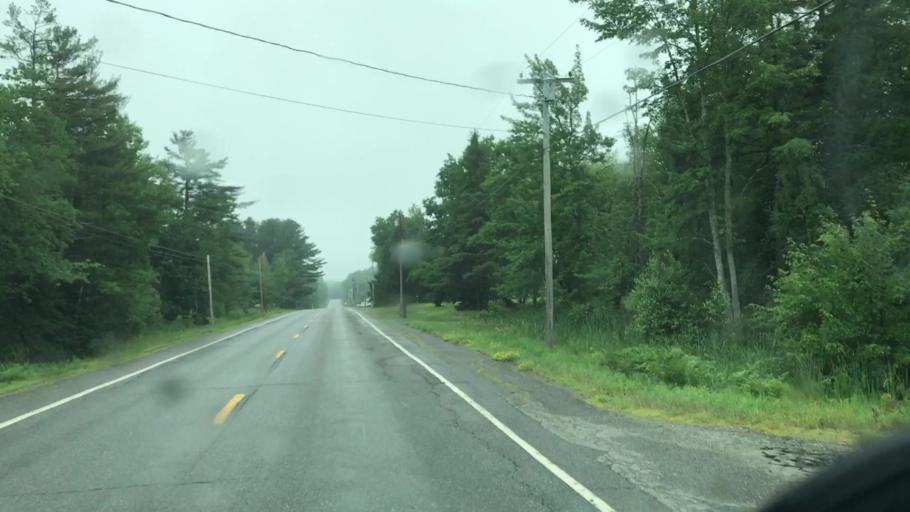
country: US
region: Maine
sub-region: Penobscot County
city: Howland
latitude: 45.2799
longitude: -68.6310
